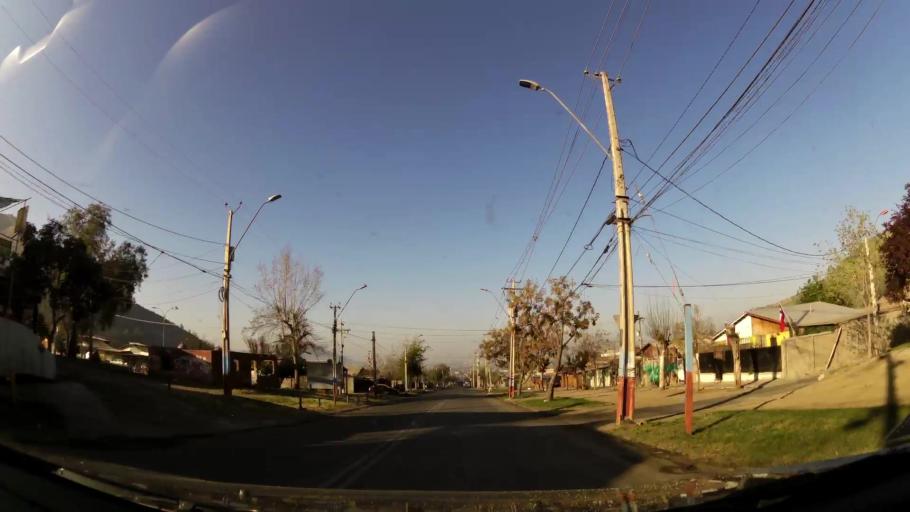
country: CL
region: Santiago Metropolitan
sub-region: Provincia de Chacabuco
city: Chicureo Abajo
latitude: -33.3602
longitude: -70.6310
